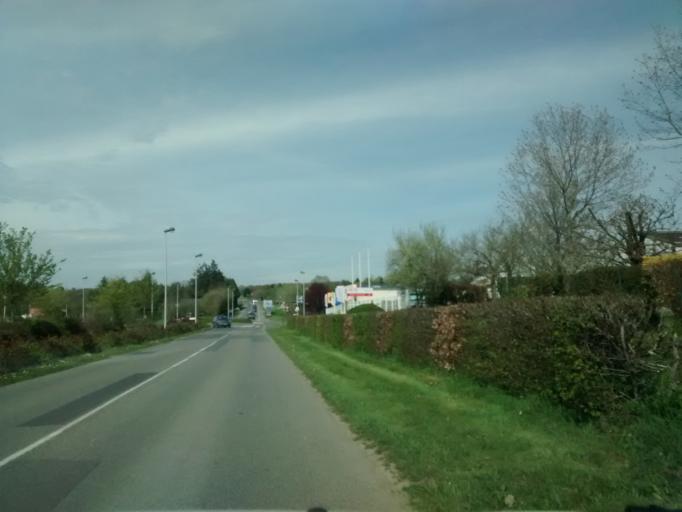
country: FR
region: Brittany
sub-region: Departement d'Ille-et-Vilaine
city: Fouillard
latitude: 48.1531
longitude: -1.5893
